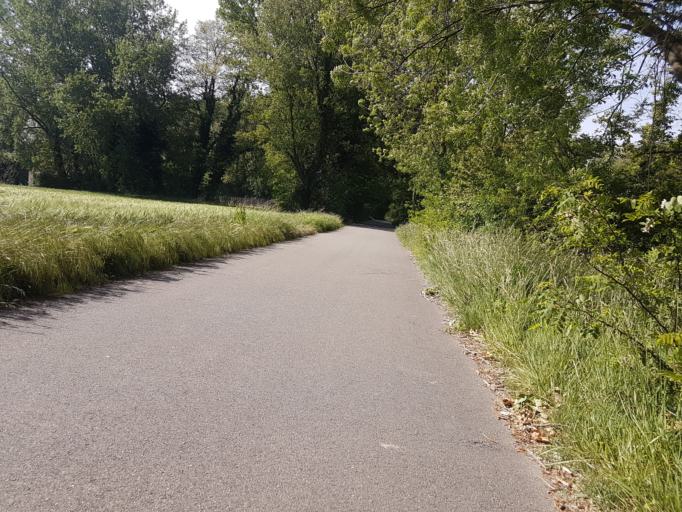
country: FR
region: Rhone-Alpes
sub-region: Departement de l'Ardeche
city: La Voulte-sur-Rhone
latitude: 44.7847
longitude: 4.7751
